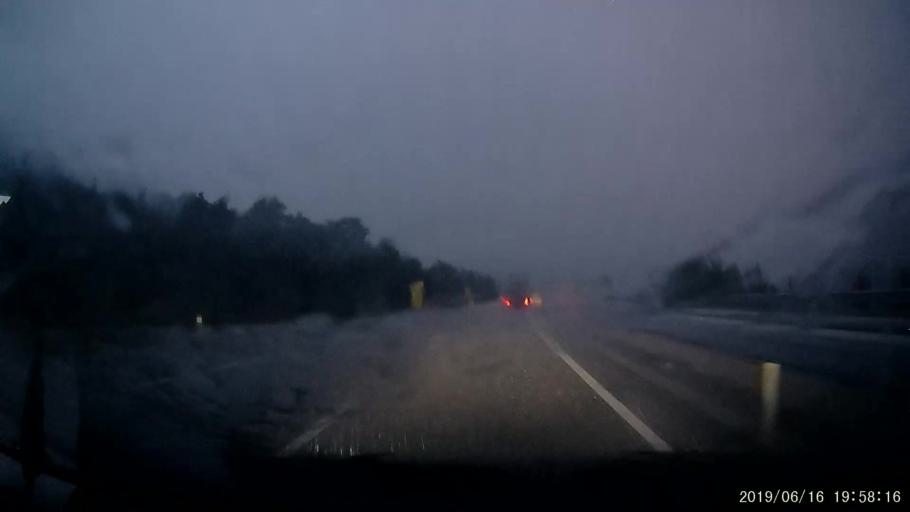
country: TR
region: Sivas
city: Koyulhisar
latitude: 40.2965
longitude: 37.7268
